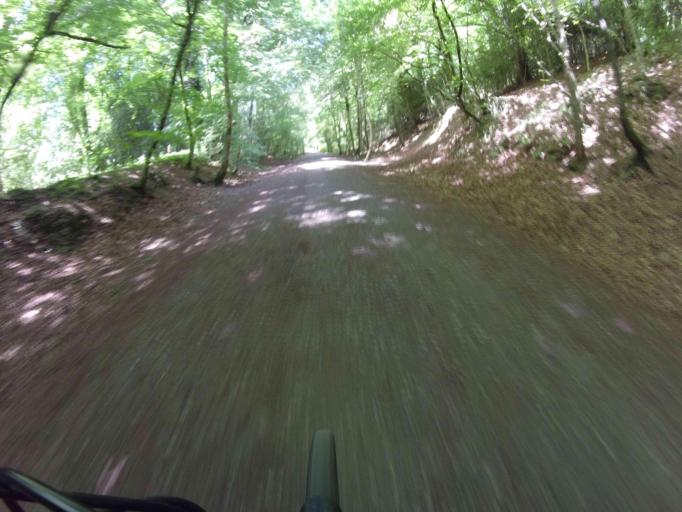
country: GB
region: England
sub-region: Devon
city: Bovey Tracey
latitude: 50.5998
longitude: -3.6922
